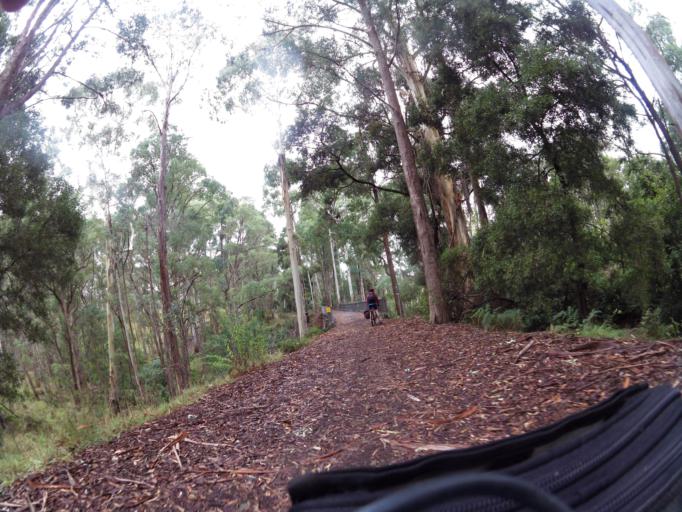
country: AU
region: New South Wales
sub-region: Greater Hume Shire
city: Holbrook
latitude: -36.1615
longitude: 147.4867
